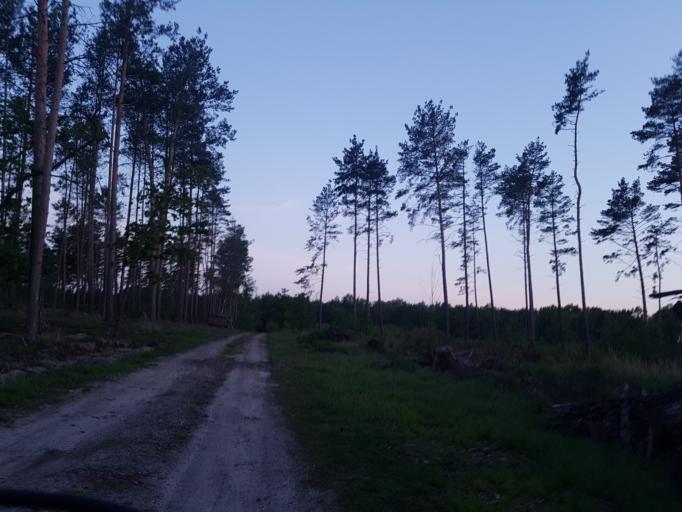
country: DE
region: Brandenburg
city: Schilda
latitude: 51.5605
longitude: 13.3725
